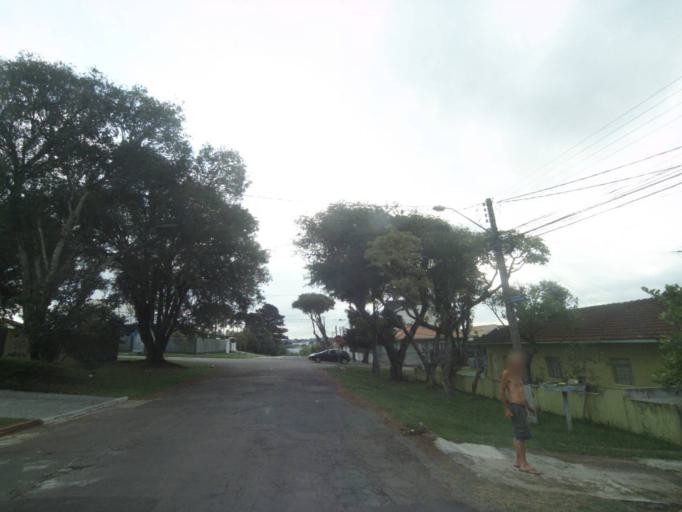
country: BR
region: Parana
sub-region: Pinhais
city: Pinhais
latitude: -25.4142
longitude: -49.2155
